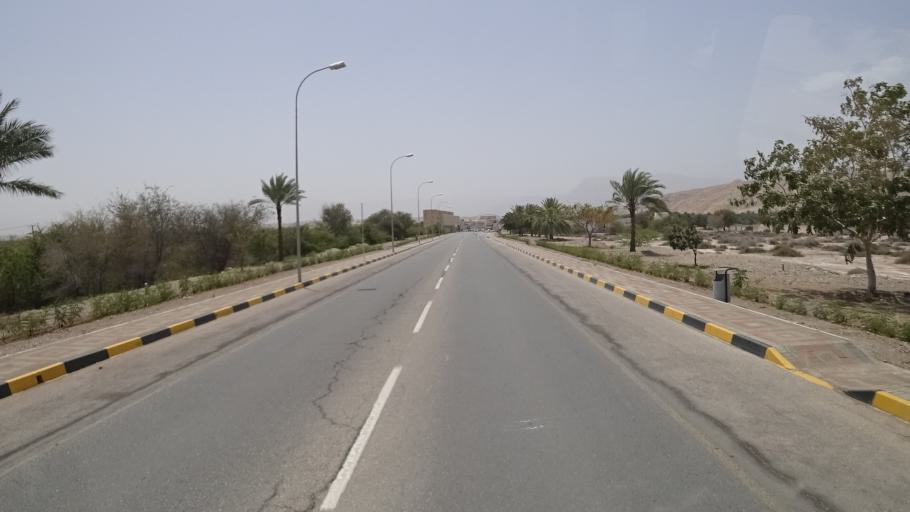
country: OM
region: Muhafazat Masqat
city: Muscat
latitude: 23.2457
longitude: 58.9045
